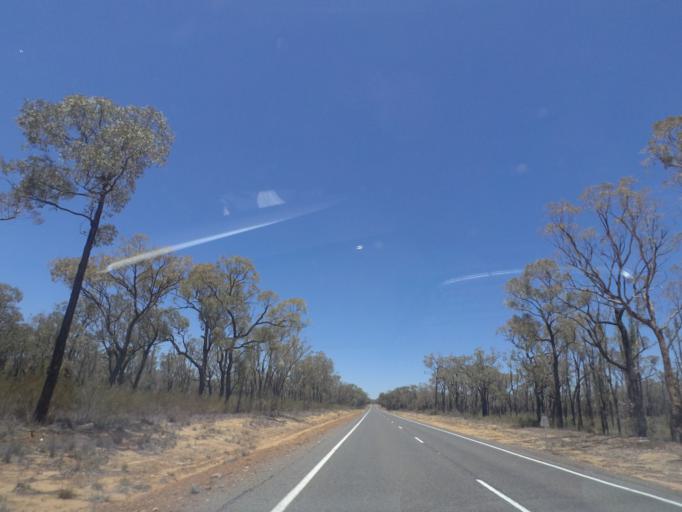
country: AU
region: New South Wales
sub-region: Narrabri
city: Narrabri
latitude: -30.7066
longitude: 149.5320
